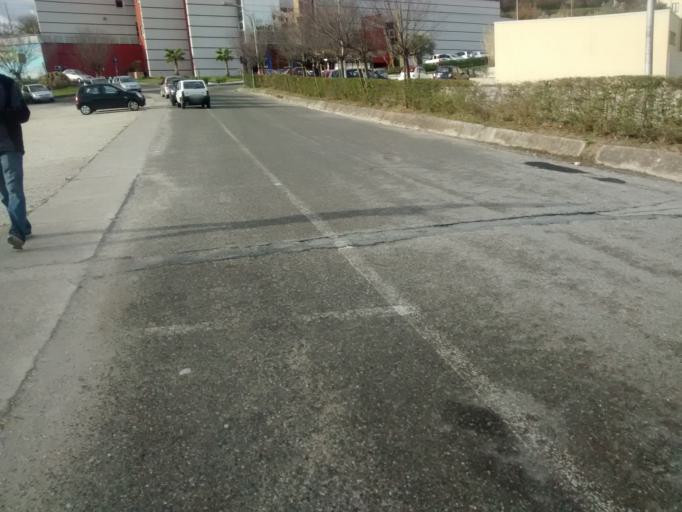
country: IT
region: Calabria
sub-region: Provincia di Cosenza
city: Arcavacata
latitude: 39.3578
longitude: 16.2260
